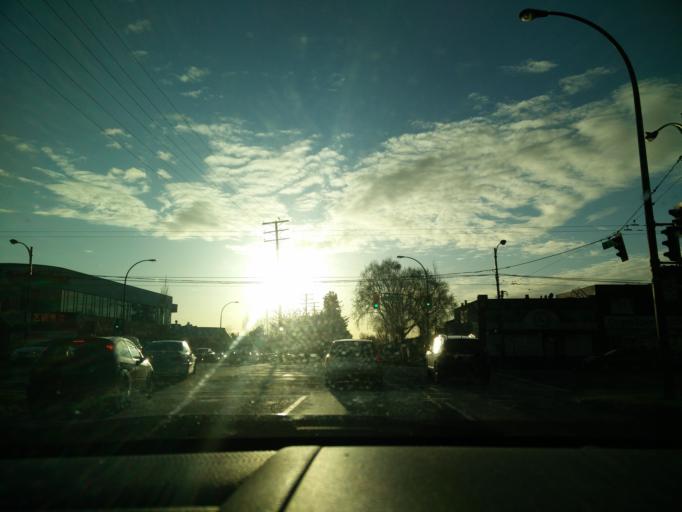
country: CA
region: British Columbia
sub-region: Fraser Valley Regional District
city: North Vancouver
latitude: 49.2696
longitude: -123.0437
